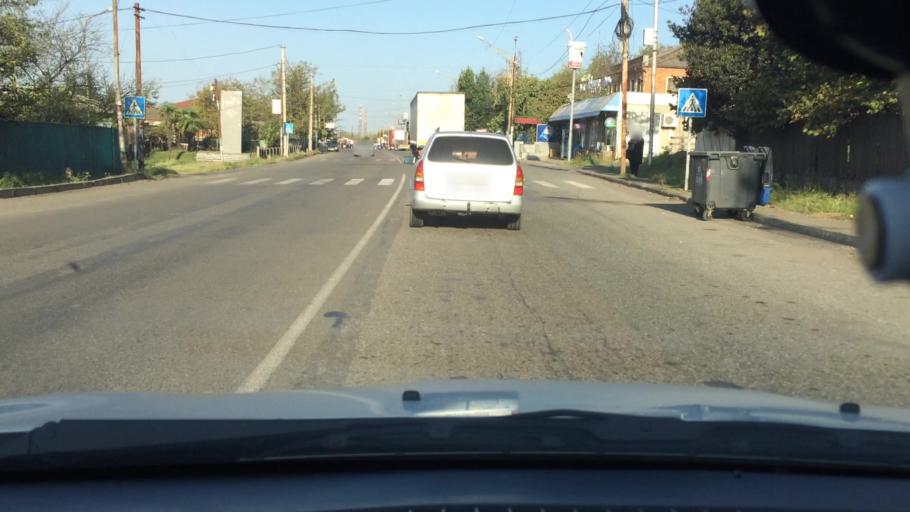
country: GE
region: Imereti
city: Zestap'oni
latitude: 42.1106
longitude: 43.0432
